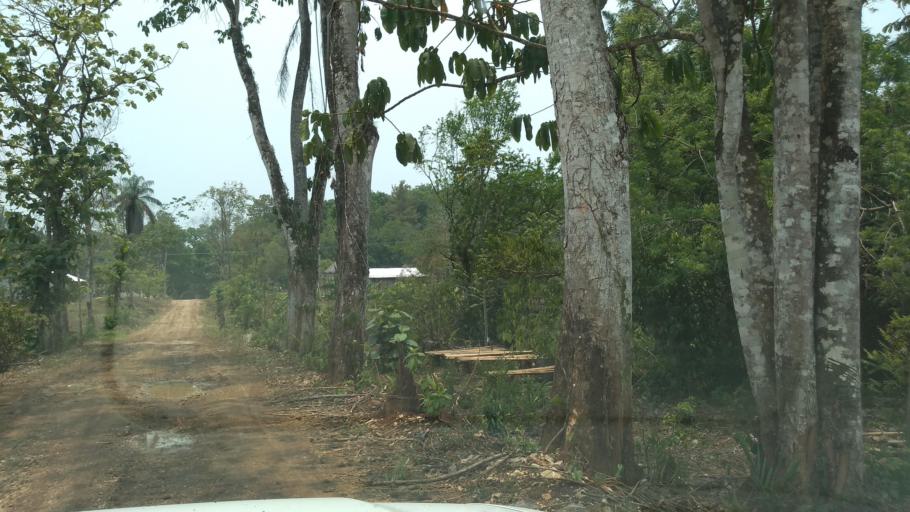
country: MX
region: Veracruz
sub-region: Tezonapa
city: Laguna Chica (Pueblo Nuevo)
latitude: 18.5128
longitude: -96.7570
